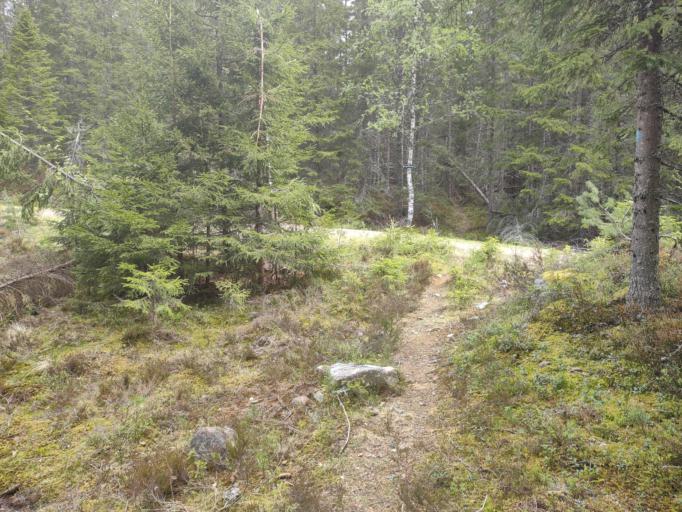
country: NO
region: Oppland
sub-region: Lunner
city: Grua
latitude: 60.3023
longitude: 10.7982
